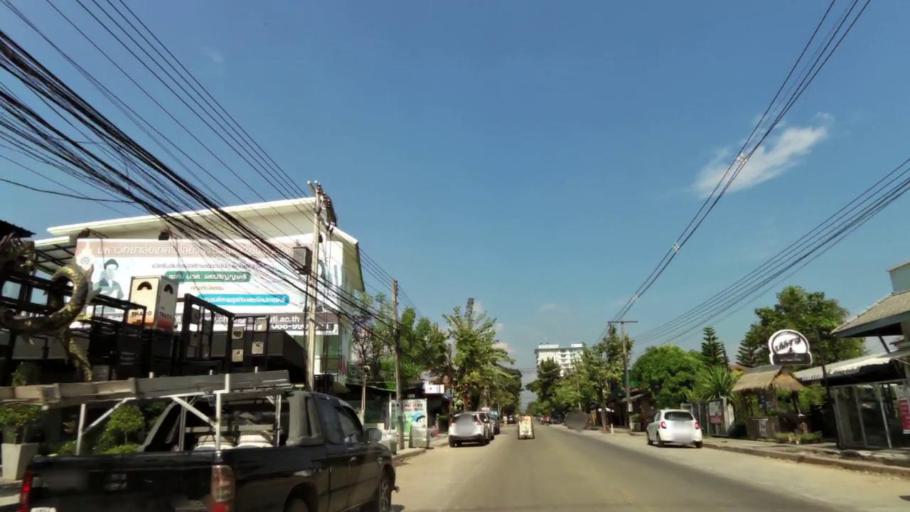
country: TH
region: Chiang Rai
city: Chiang Rai
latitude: 19.8964
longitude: 99.8276
